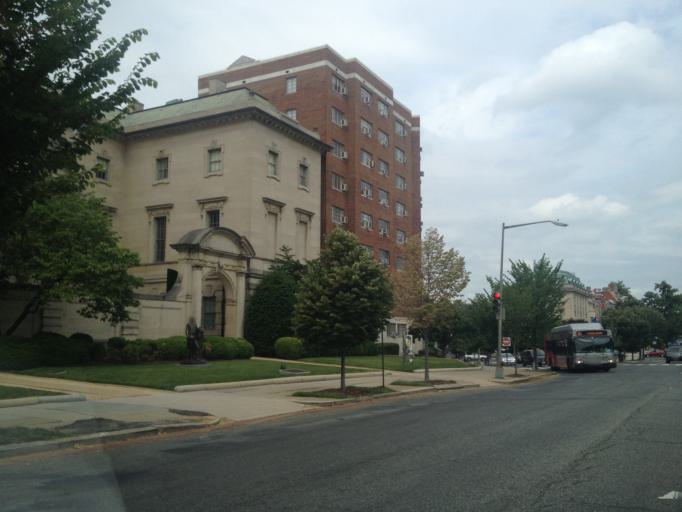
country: US
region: Washington, D.C.
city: Washington, D.C.
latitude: 38.9110
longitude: -77.0473
